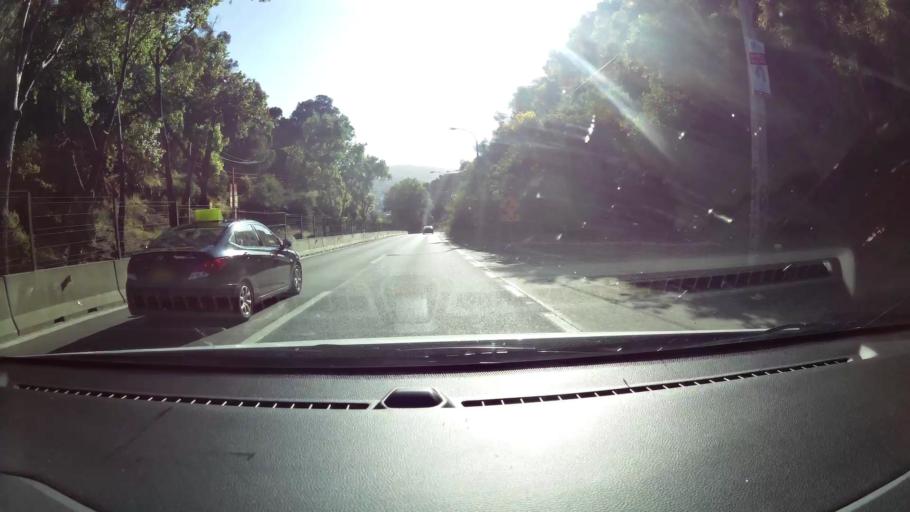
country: CL
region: Valparaiso
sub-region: Provincia de Valparaiso
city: Valparaiso
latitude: -33.0504
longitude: -71.5918
